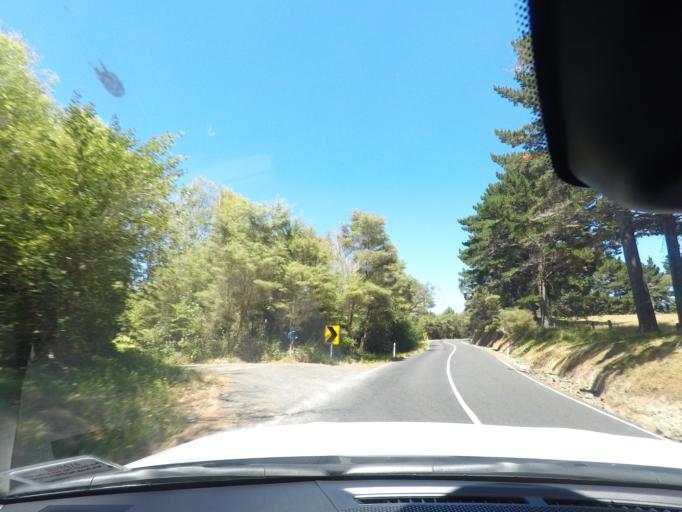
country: NZ
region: Auckland
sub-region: Auckland
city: Parakai
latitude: -36.5758
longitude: 174.3550
